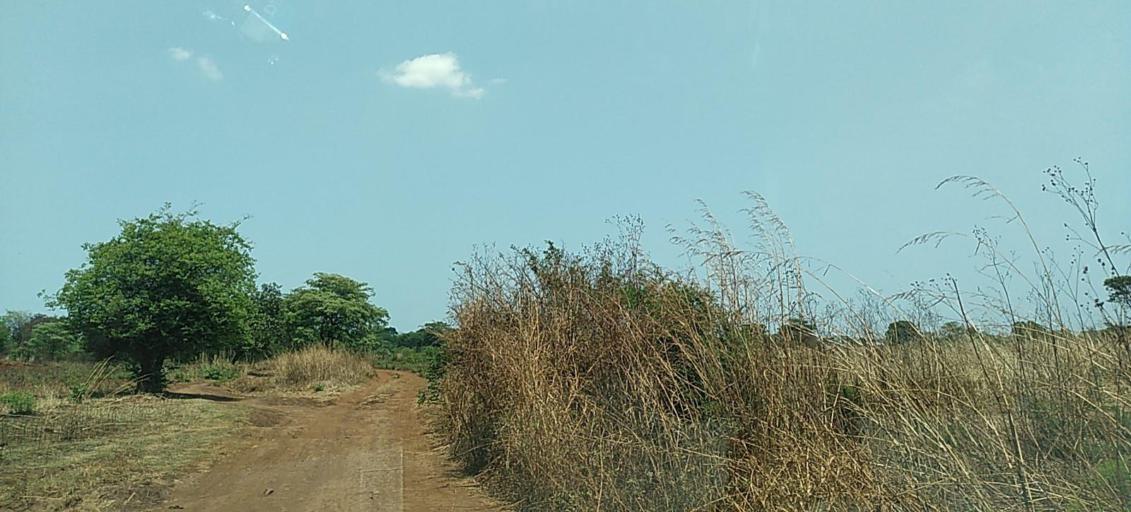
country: ZM
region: Copperbelt
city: Mpongwe
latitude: -13.8374
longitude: 27.8408
